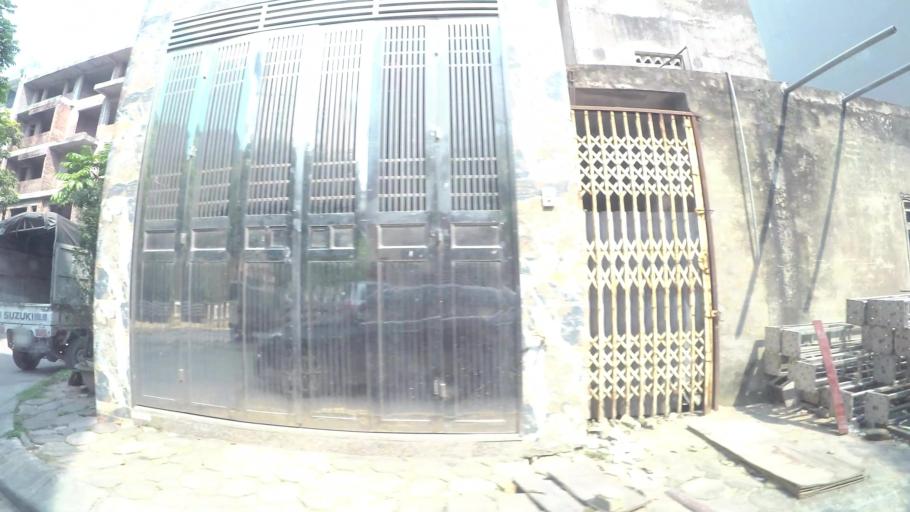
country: VN
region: Ha Noi
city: Ha Dong
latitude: 20.9553
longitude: 105.8083
